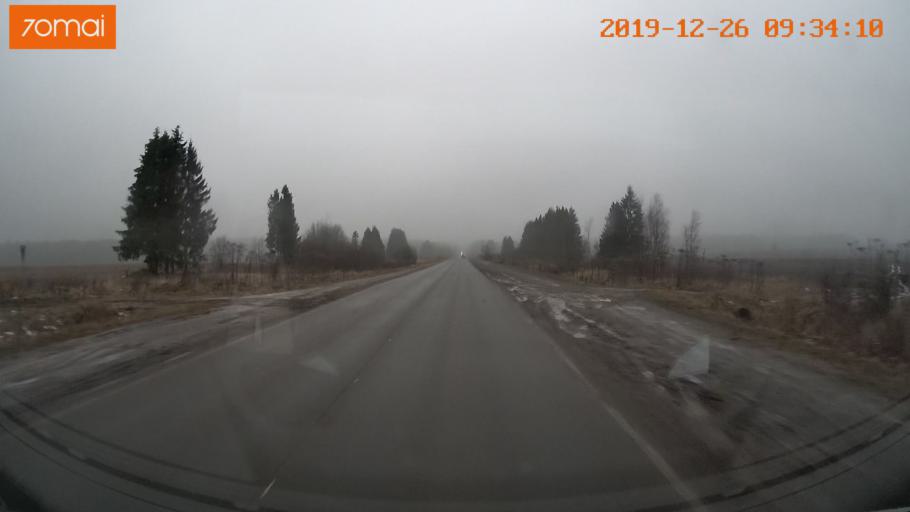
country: RU
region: Vologda
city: Vologda
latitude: 59.0983
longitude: 40.0899
